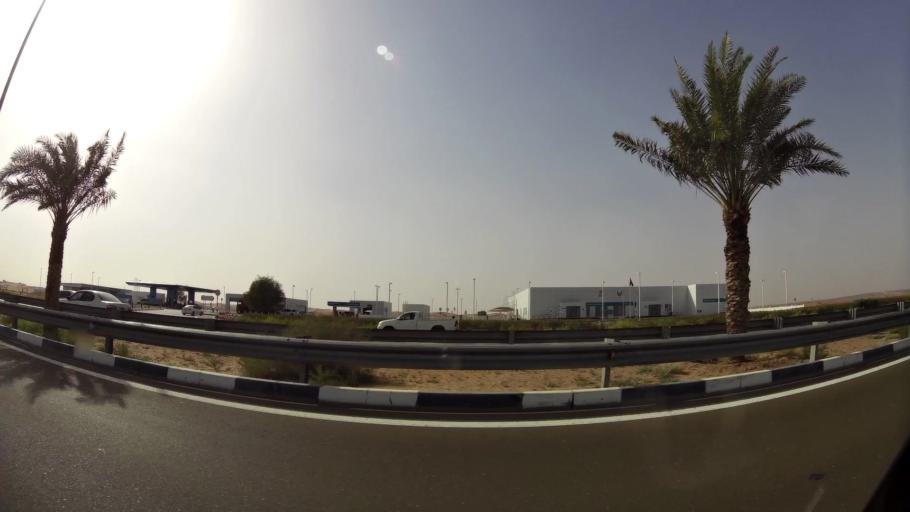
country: AE
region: Abu Dhabi
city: Al Ain
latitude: 24.2187
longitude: 55.6400
